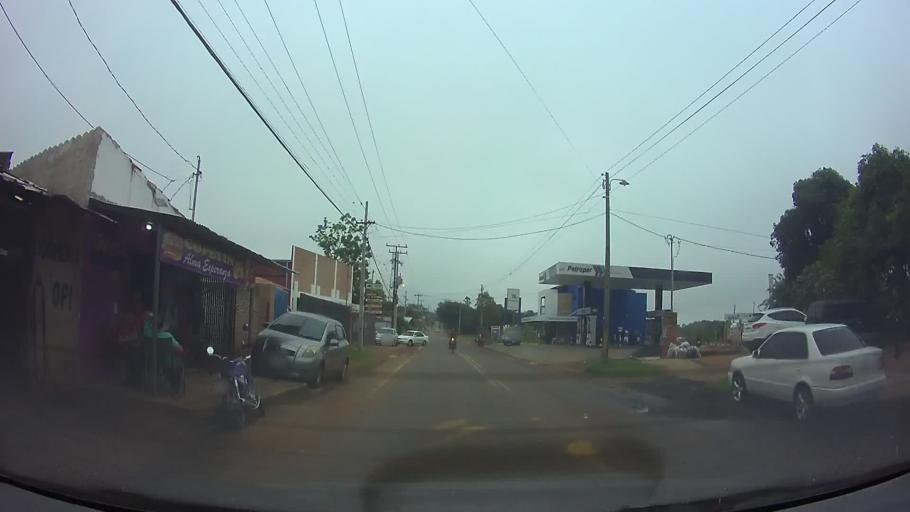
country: PY
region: Central
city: Itaugua
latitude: -25.3839
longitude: -57.3505
